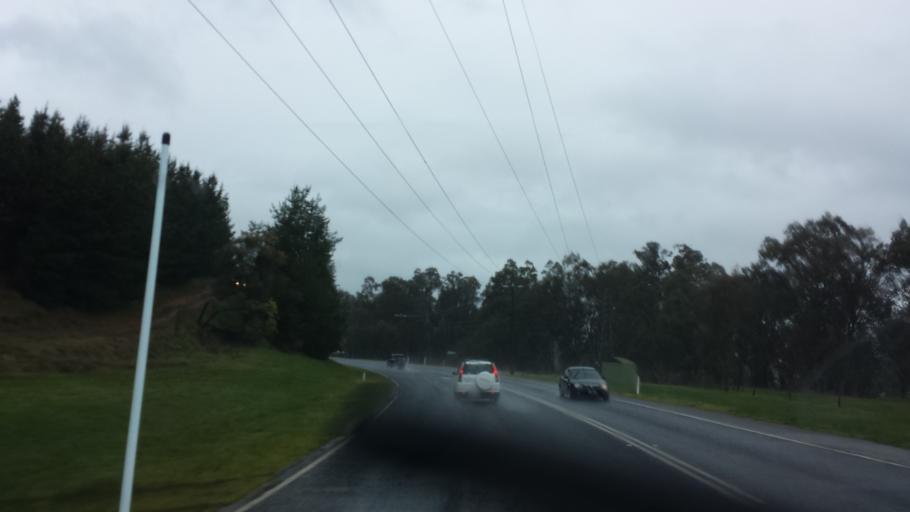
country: AU
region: Victoria
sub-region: Alpine
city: Mount Beauty
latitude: -36.5809
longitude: 146.7509
